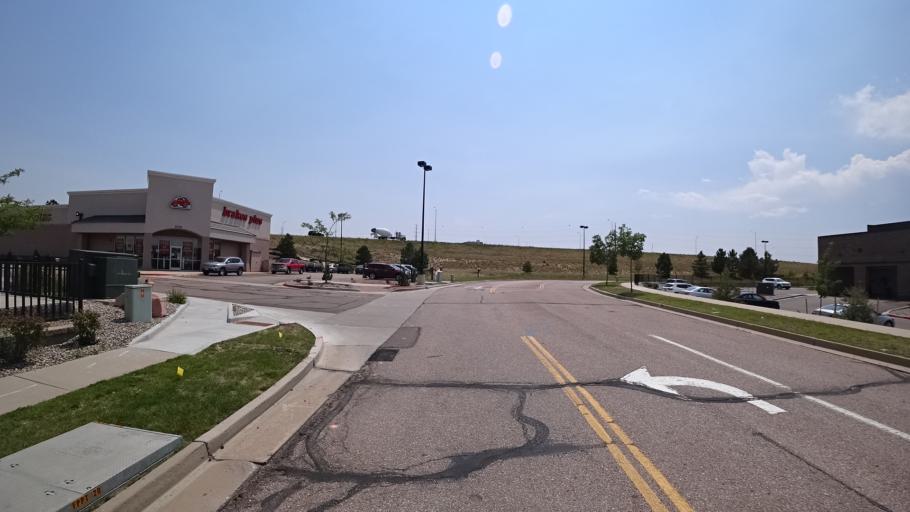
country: US
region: Colorado
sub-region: El Paso County
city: Black Forest
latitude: 38.9437
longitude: -104.7214
